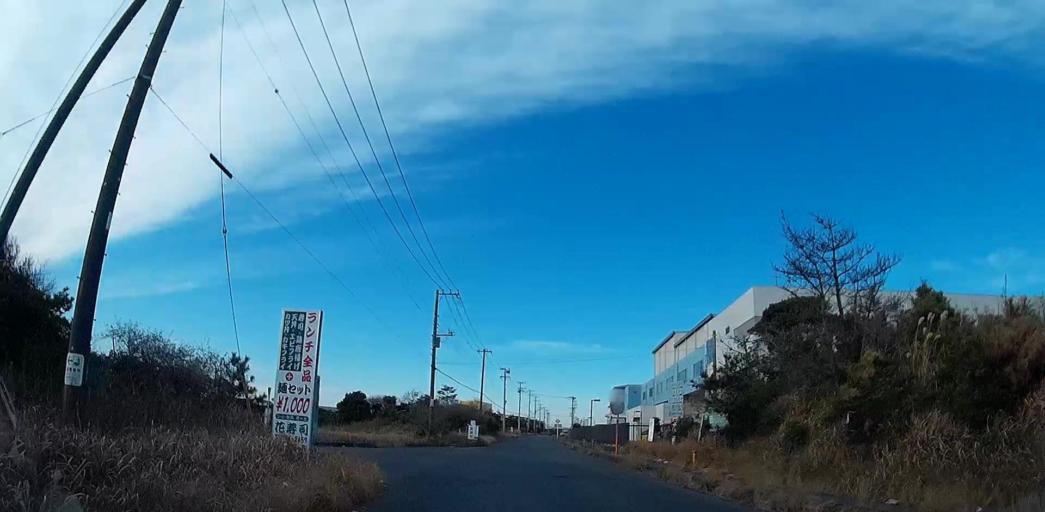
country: JP
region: Chiba
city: Hasaki
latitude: 35.7659
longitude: 140.8180
